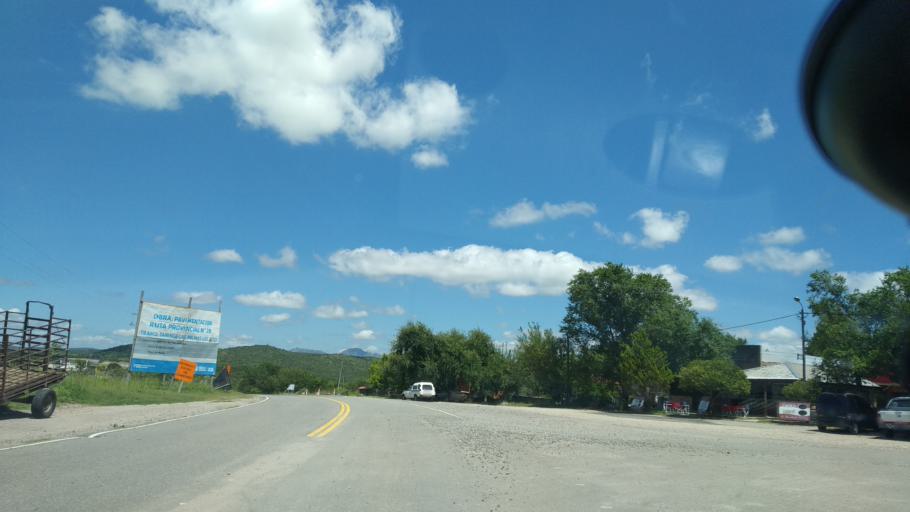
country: AR
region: Cordoba
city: Salsacate
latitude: -31.3460
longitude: -65.0802
